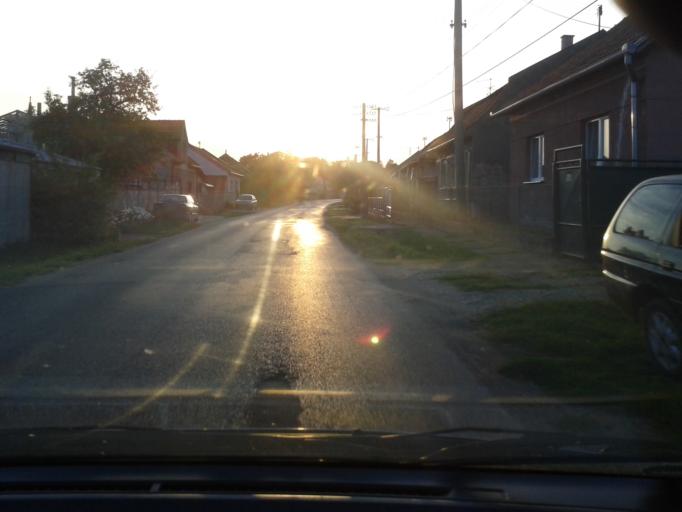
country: HU
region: Komarom-Esztergom
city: Esztergom
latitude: 47.8278
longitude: 18.7360
